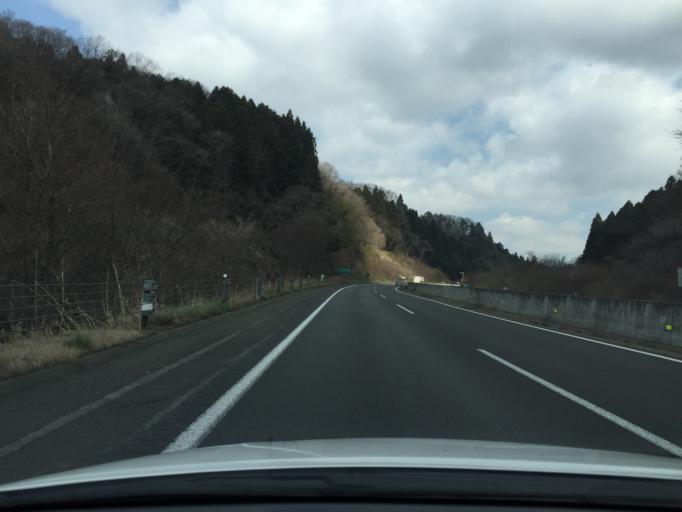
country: JP
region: Miyagi
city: Sendai
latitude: 38.2417
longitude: 140.8178
